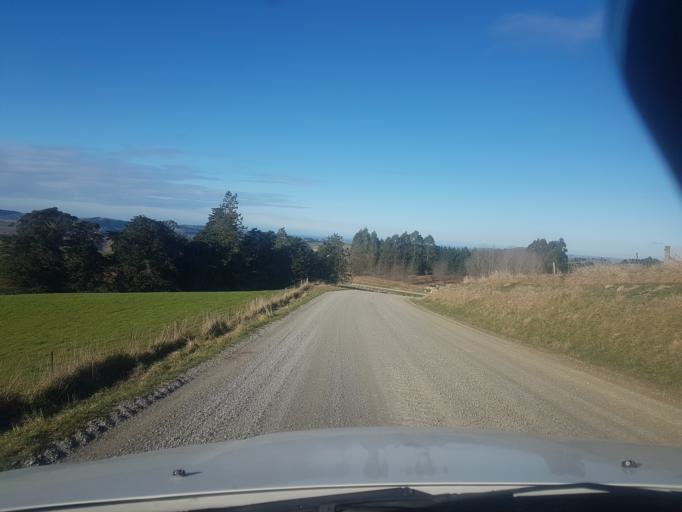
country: NZ
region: Canterbury
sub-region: Timaru District
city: Pleasant Point
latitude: -44.1679
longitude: 170.9169
